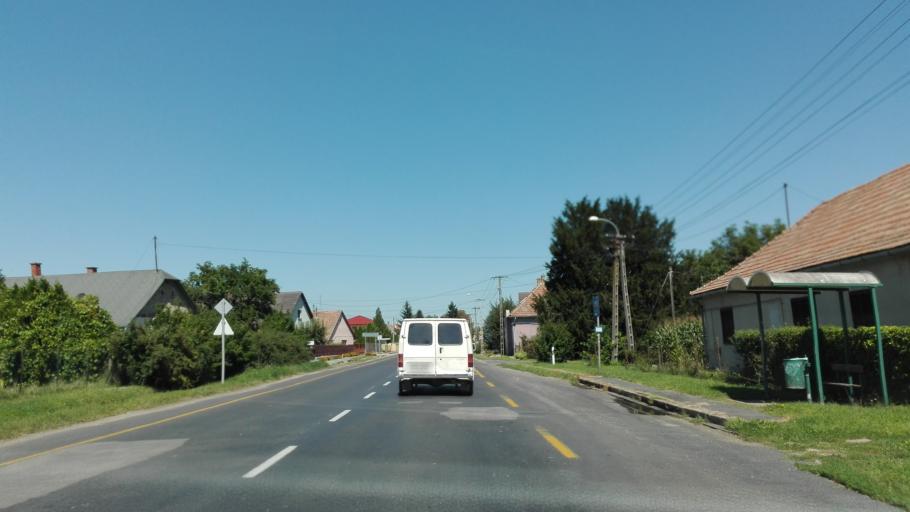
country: HU
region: Fejer
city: Mezoszilas
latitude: 46.8062
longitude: 18.4862
